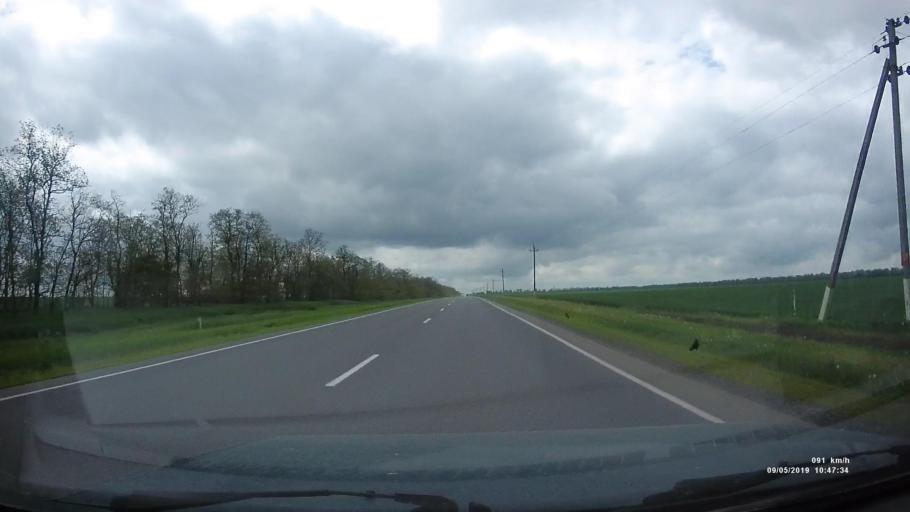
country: RU
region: Rostov
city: Peshkovo
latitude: 46.9690
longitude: 39.3556
